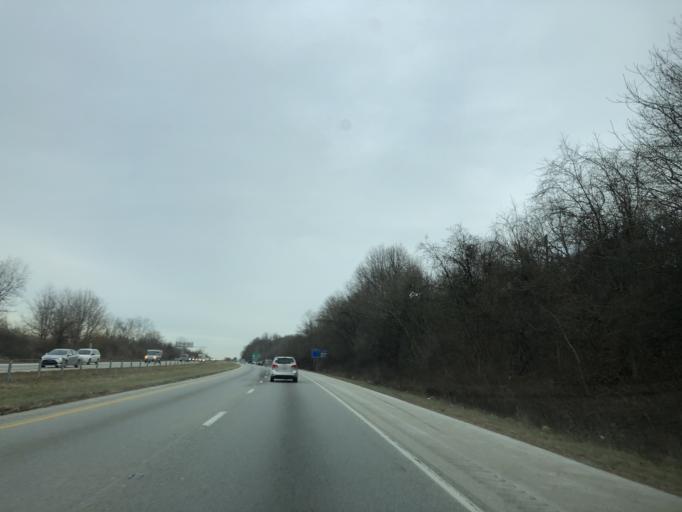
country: US
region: Pennsylvania
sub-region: Chester County
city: Exton
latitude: 40.0137
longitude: -75.6435
